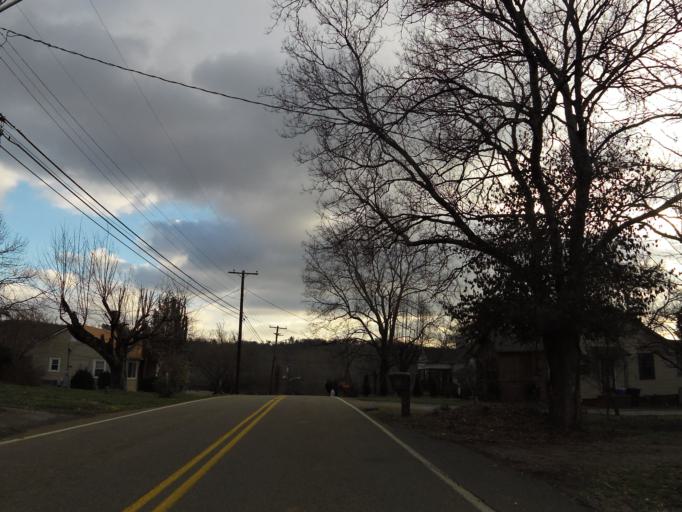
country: US
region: Tennessee
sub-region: Knox County
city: Knoxville
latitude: 35.9440
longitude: -83.8909
